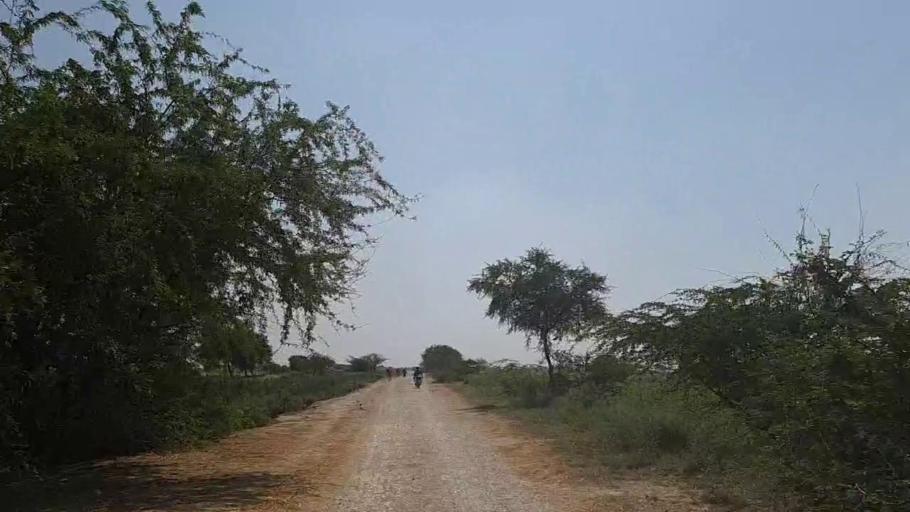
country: PK
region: Sindh
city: Mirpur Batoro
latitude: 24.5509
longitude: 68.3171
